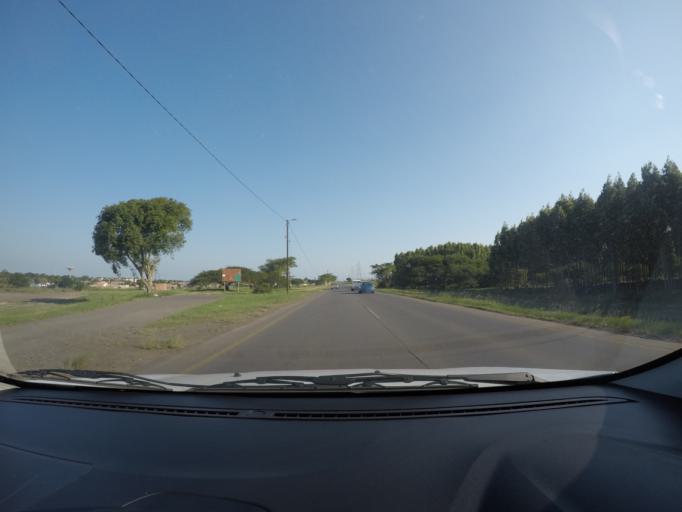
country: ZA
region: KwaZulu-Natal
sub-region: uThungulu District Municipality
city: Richards Bay
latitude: -28.7207
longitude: 32.0331
